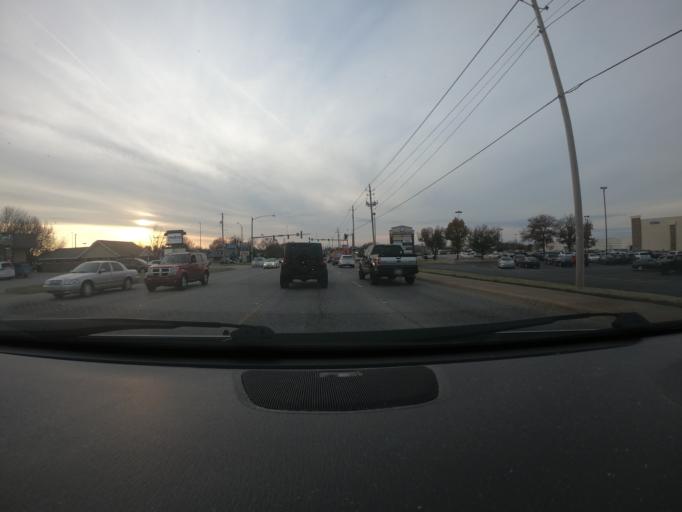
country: US
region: Arkansas
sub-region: Benton County
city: Rogers
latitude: 36.3341
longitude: -94.1465
